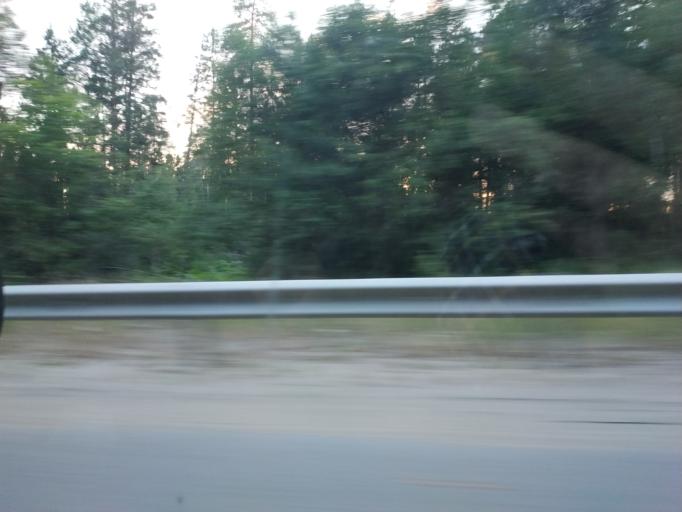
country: RU
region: Moskovskaya
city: Krasnoarmeysk
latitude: 56.0305
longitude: 38.1848
